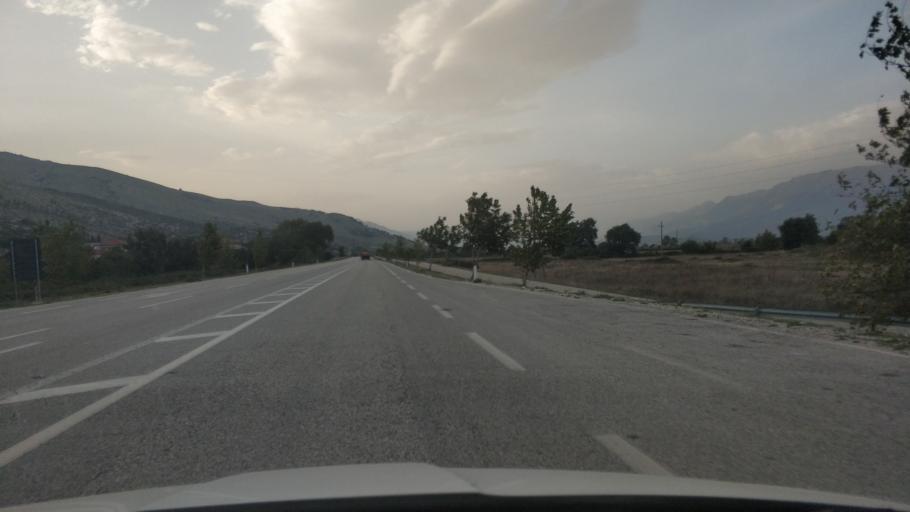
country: AL
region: Gjirokaster
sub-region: Rrethi i Gjirokastres
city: Libohove
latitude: 39.9526
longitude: 20.2537
